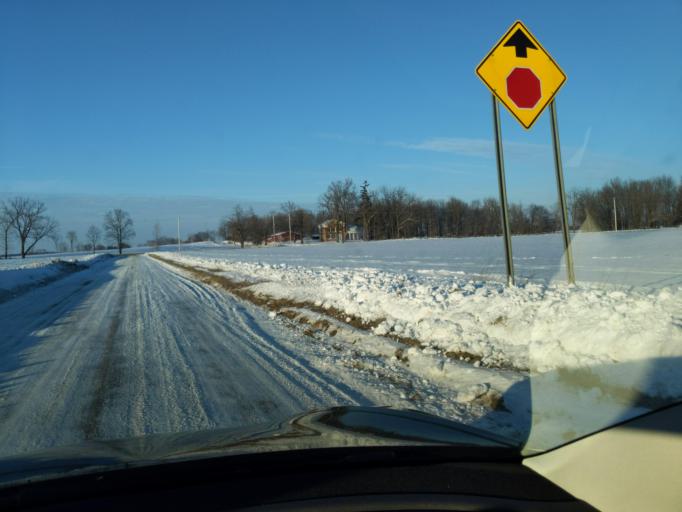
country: US
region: Michigan
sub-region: Ingham County
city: Stockbridge
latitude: 42.4951
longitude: -84.1194
